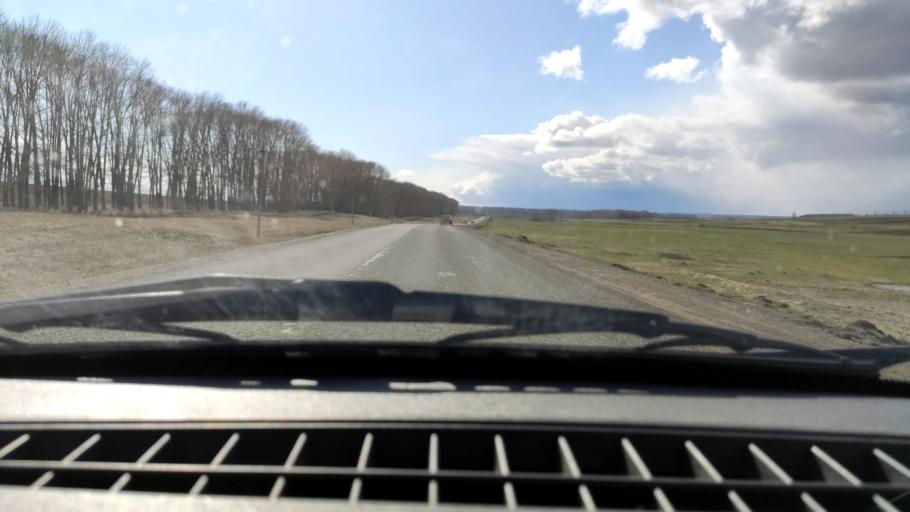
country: RU
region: Bashkortostan
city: Chekmagush
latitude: 55.1166
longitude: 54.7735
